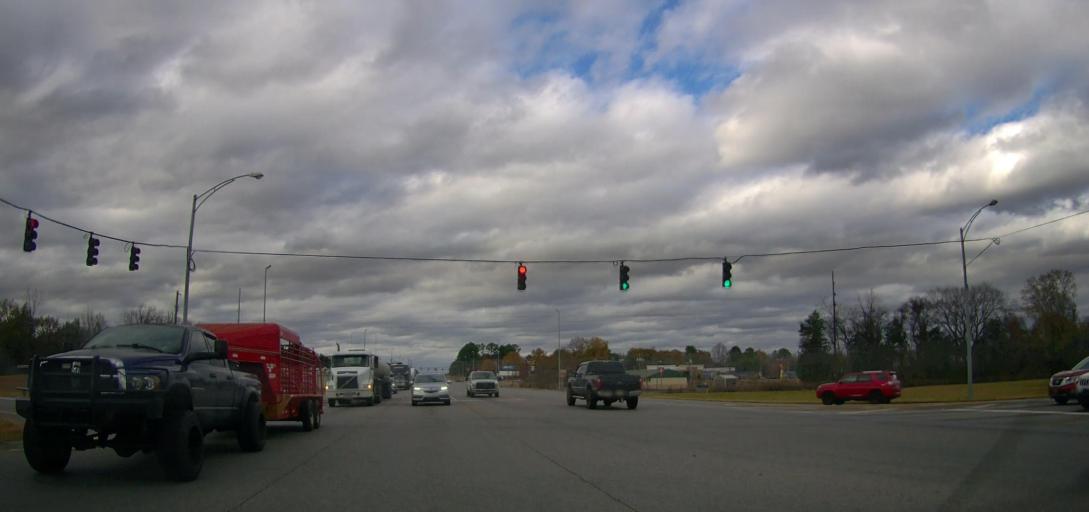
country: US
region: Alabama
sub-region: Lawrence County
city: Moulton
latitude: 34.4923
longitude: -87.2789
